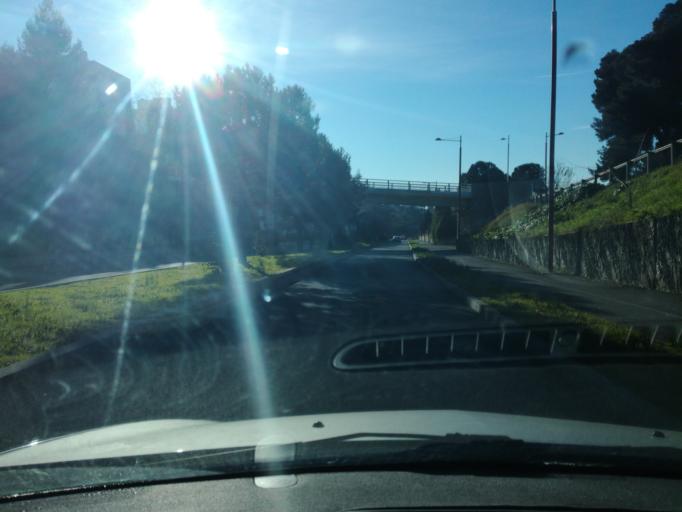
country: FR
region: Provence-Alpes-Cote d'Azur
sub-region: Departement des Alpes-Maritimes
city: Biot
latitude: 43.5941
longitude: 7.0911
